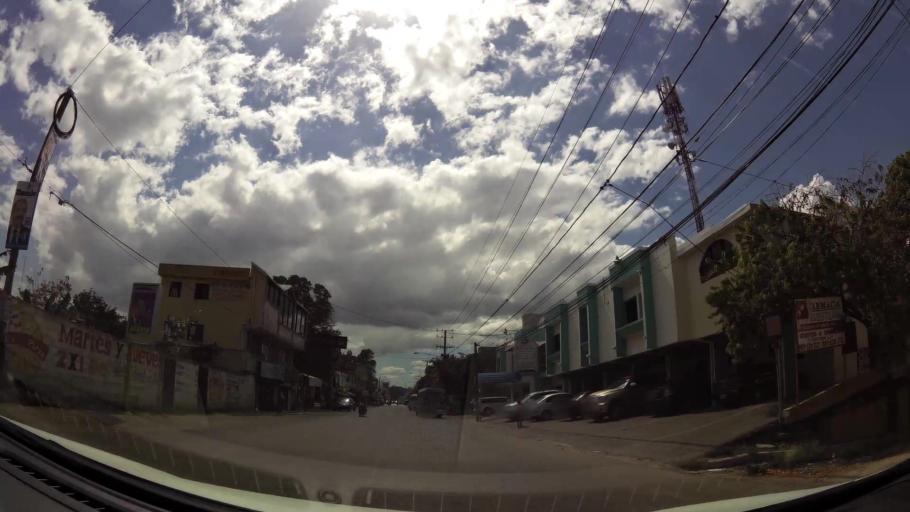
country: DO
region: San Cristobal
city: San Cristobal
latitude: 18.4212
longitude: -70.0990
